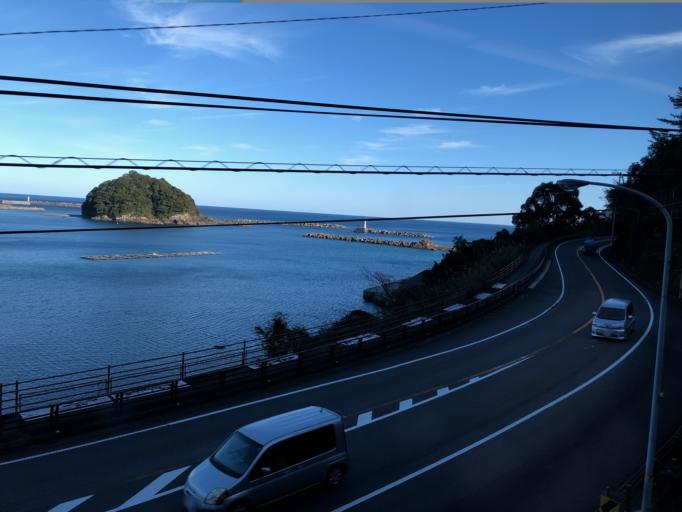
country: JP
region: Kochi
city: Nakamura
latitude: 33.0710
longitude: 133.1041
